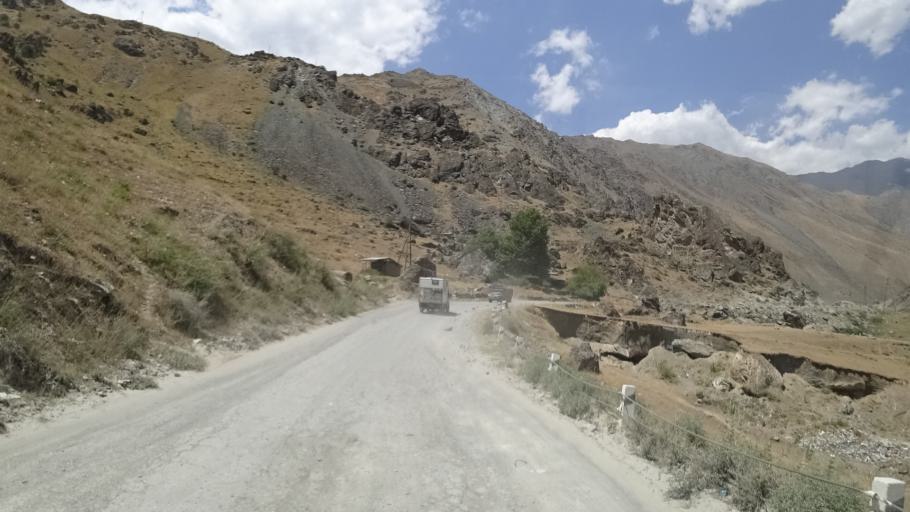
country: AF
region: Badakhshan
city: Nusay
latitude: 38.4504
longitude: 70.8564
